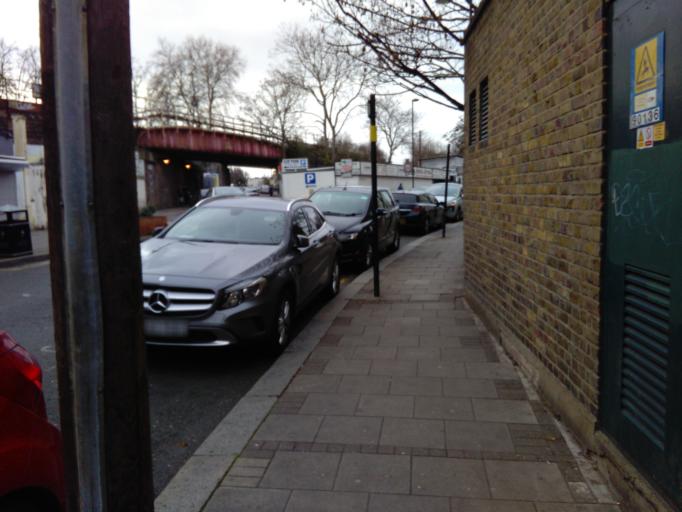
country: GB
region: England
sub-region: Greater London
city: Brixton
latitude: 51.4639
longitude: -0.1163
